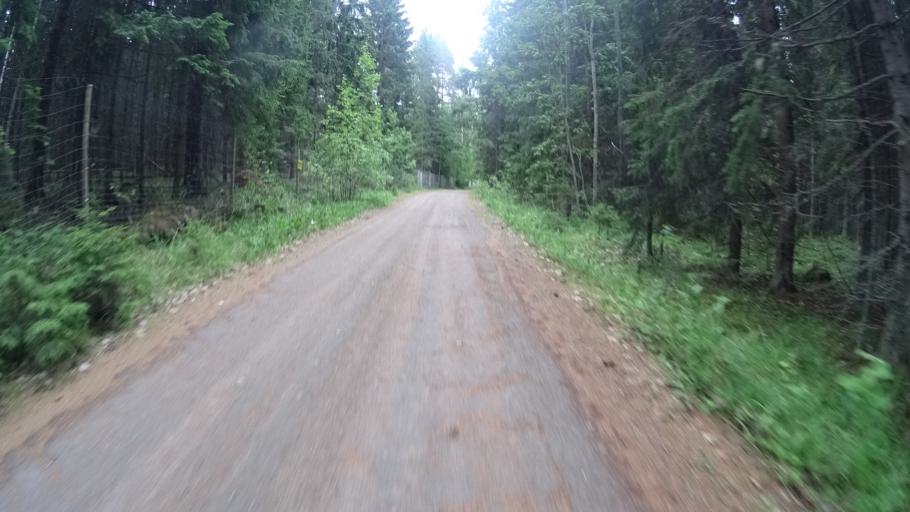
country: FI
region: Uusimaa
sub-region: Helsinki
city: Karkkila
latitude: 60.5978
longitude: 24.1343
